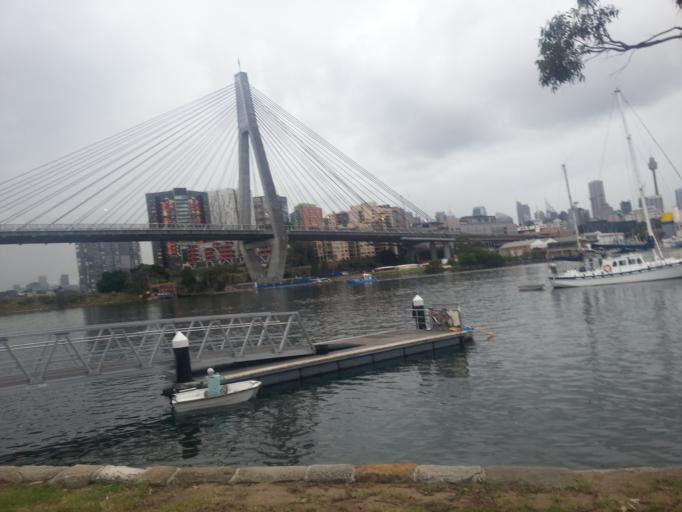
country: AU
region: New South Wales
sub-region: Leichhardt
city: Balmain East
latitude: -33.8715
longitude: 151.1850
